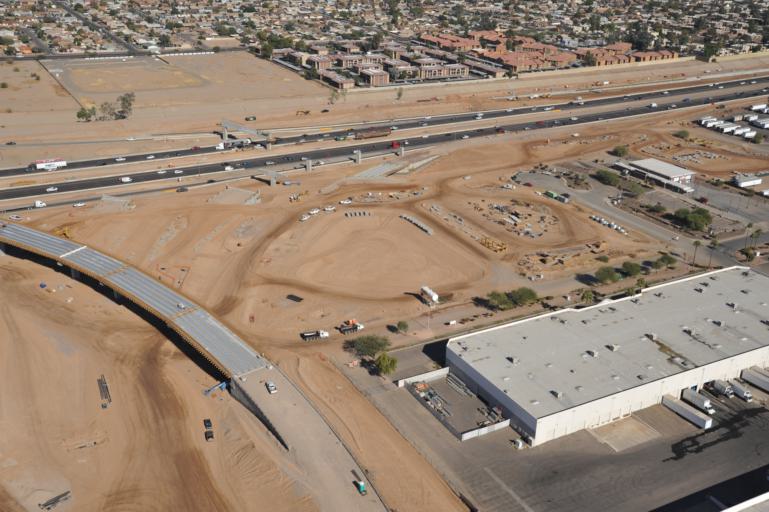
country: US
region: Arizona
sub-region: Maricopa County
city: Tolleson
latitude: 33.4583
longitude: -112.1854
